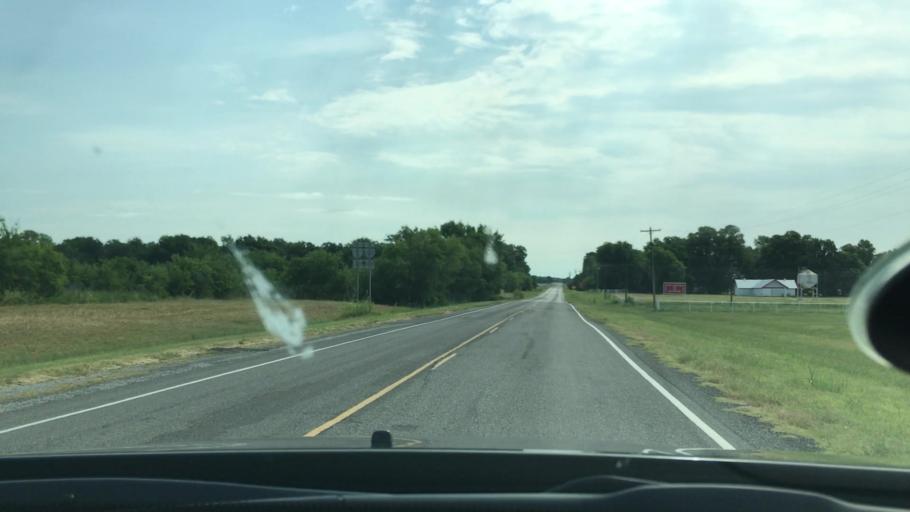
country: US
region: Oklahoma
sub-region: Carter County
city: Ardmore
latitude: 34.3327
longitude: -97.1496
